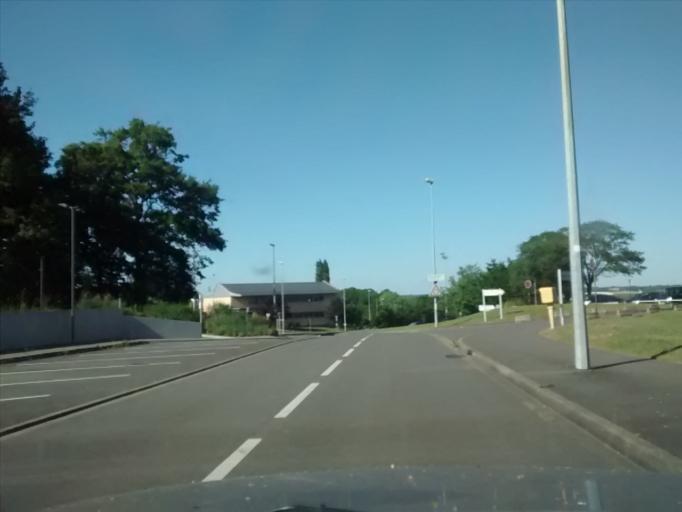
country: FR
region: Pays de la Loire
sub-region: Departement de la Sarthe
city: La Chapelle-Saint-Aubin
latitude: 48.0159
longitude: 0.1646
